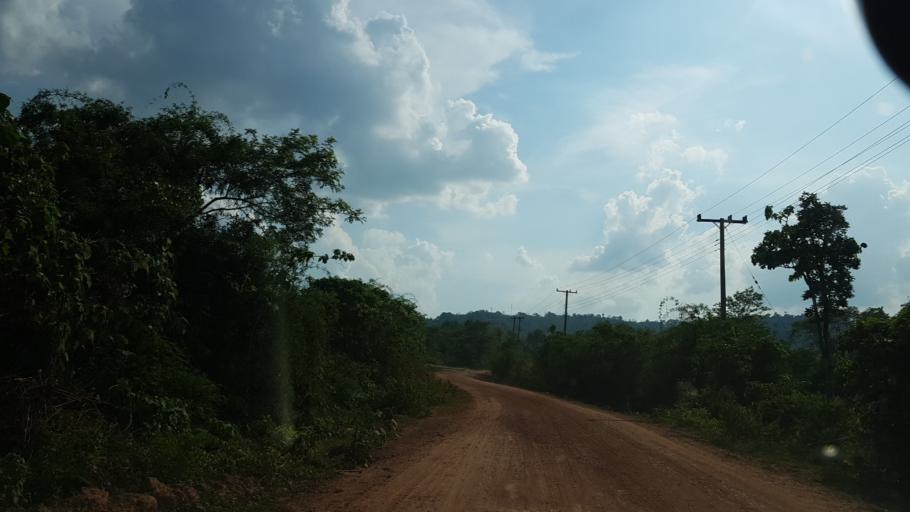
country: LA
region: Vientiane
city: Muang Phon-Hong
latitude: 18.3510
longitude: 102.2743
